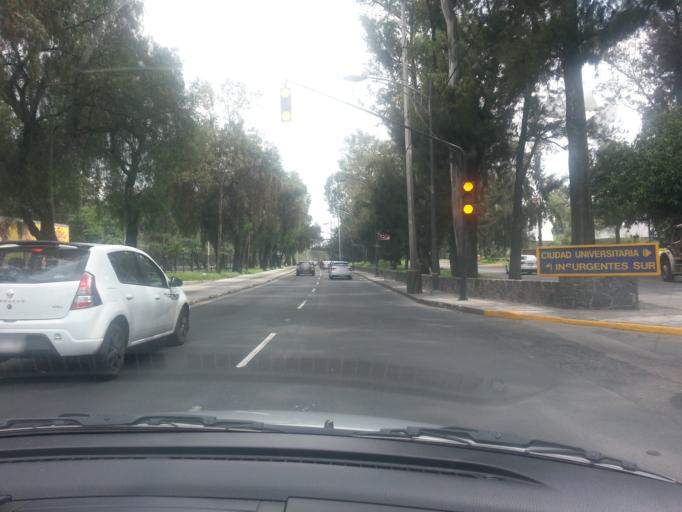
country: MX
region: Mexico City
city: Magdalena Contreras
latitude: 19.3304
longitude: -99.1896
